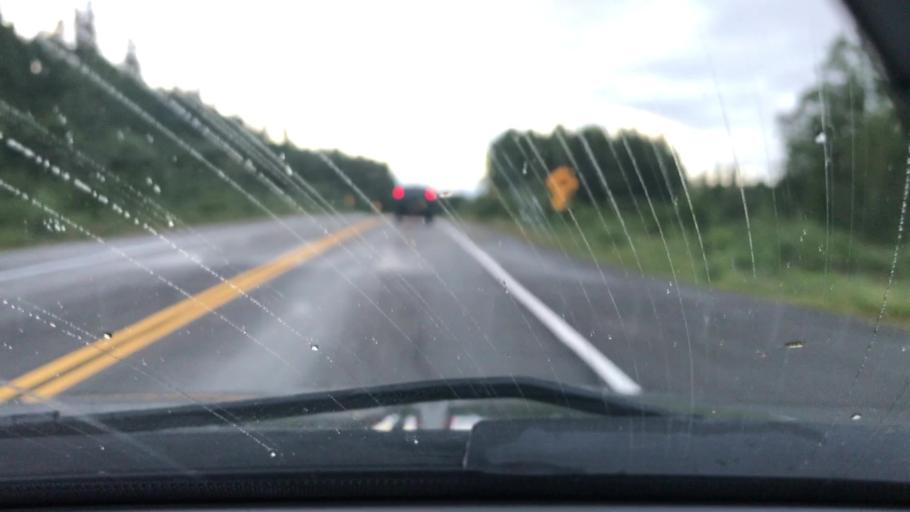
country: US
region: Alaska
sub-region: Matanuska-Susitna Borough
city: Y
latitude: 63.0426
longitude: -149.5828
